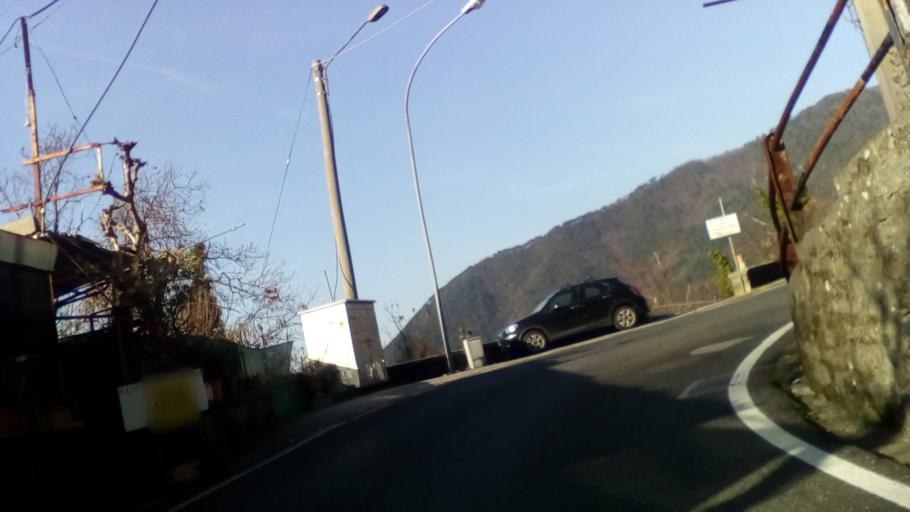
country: IT
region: Tuscany
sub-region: Provincia di Massa-Carrara
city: Montignoso
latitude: 44.0574
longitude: 10.1822
